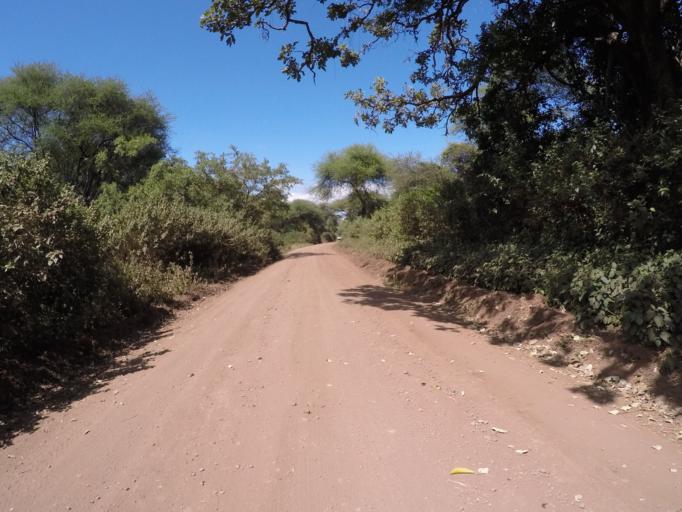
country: TZ
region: Arusha
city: Mto wa Mbu
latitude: -3.4204
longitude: 35.8142
